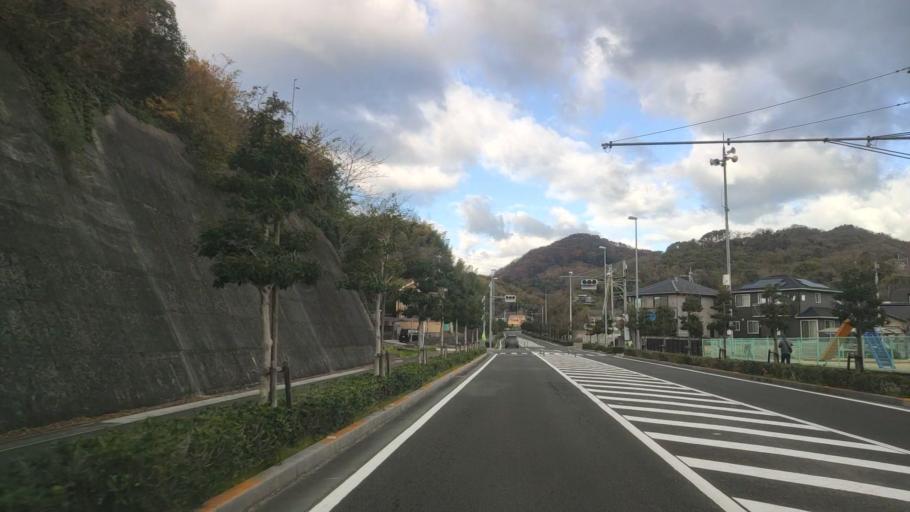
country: JP
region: Ehime
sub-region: Shikoku-chuo Shi
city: Matsuyama
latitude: 33.8729
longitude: 132.7182
